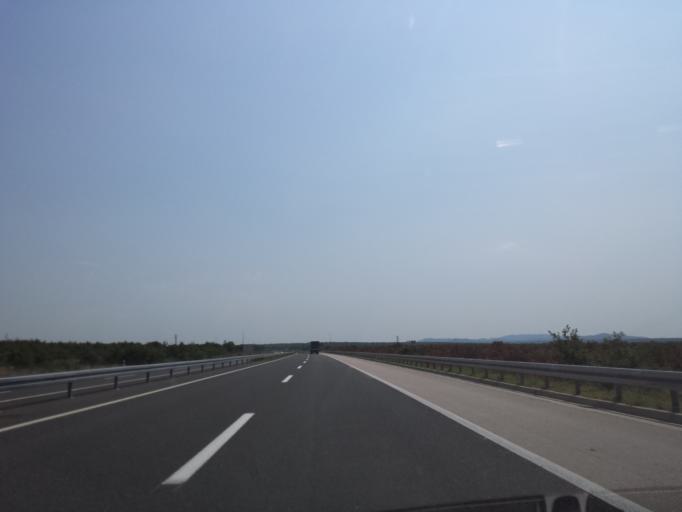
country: HR
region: Zadarska
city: Benkovac
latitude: 44.0249
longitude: 15.5694
